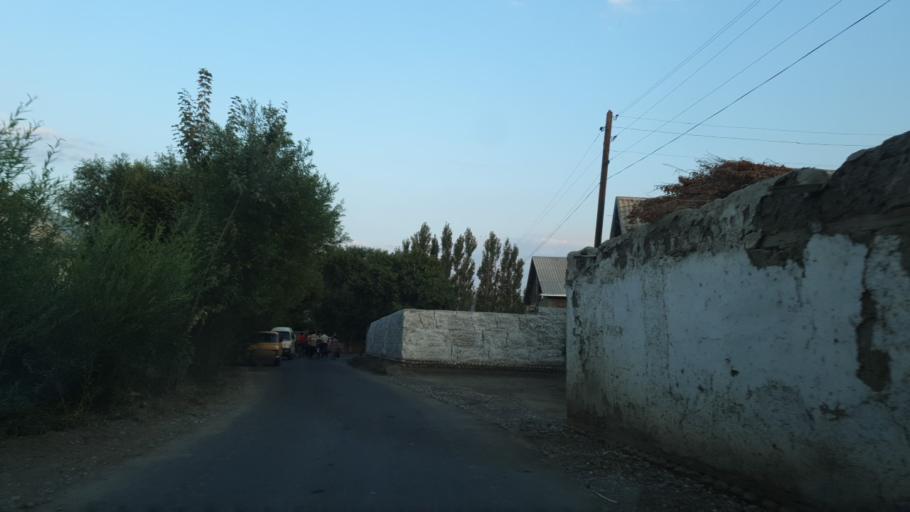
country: UZ
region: Fergana
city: Beshariq
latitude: 40.4958
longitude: 70.6218
